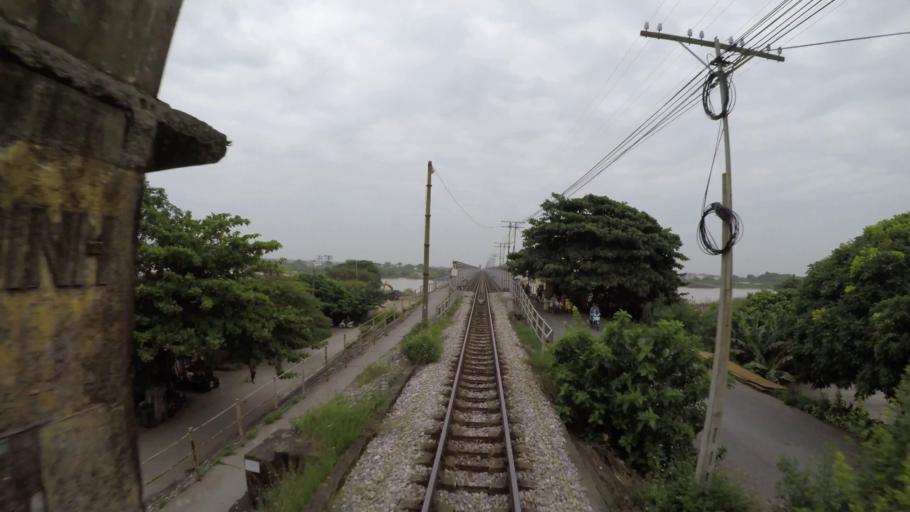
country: VN
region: Hai Duong
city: Thanh Pho Hai Duong
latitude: 20.9543
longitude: 106.3633
